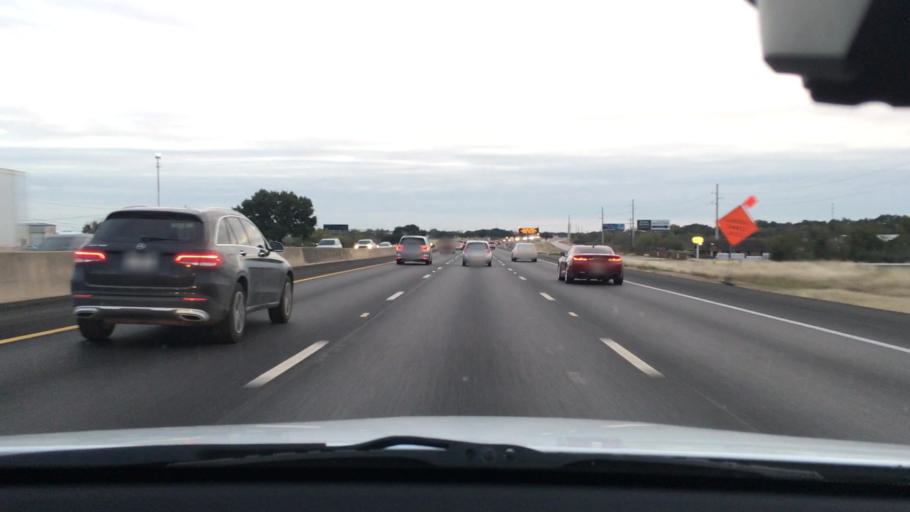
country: US
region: Texas
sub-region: Hays County
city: Kyle
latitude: 29.9727
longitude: -97.8746
